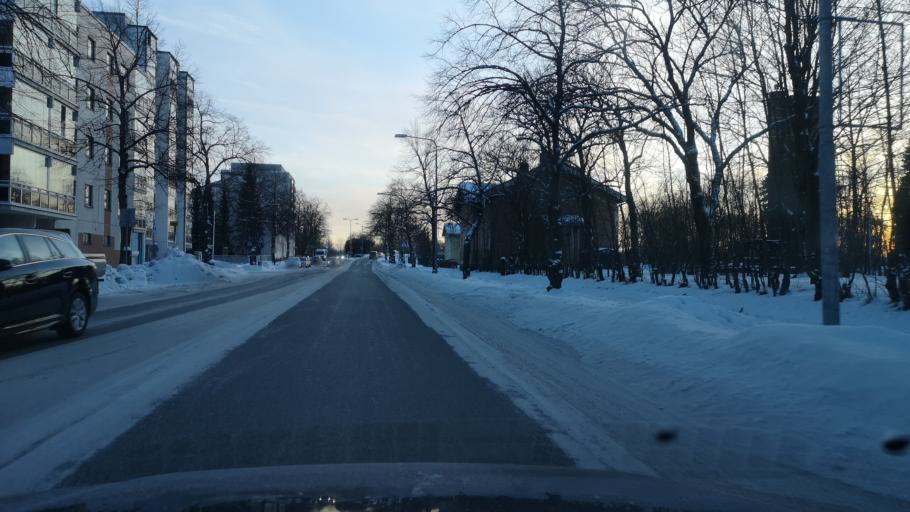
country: FI
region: Satakunta
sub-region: Pori
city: Pori
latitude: 61.4861
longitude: 21.7834
